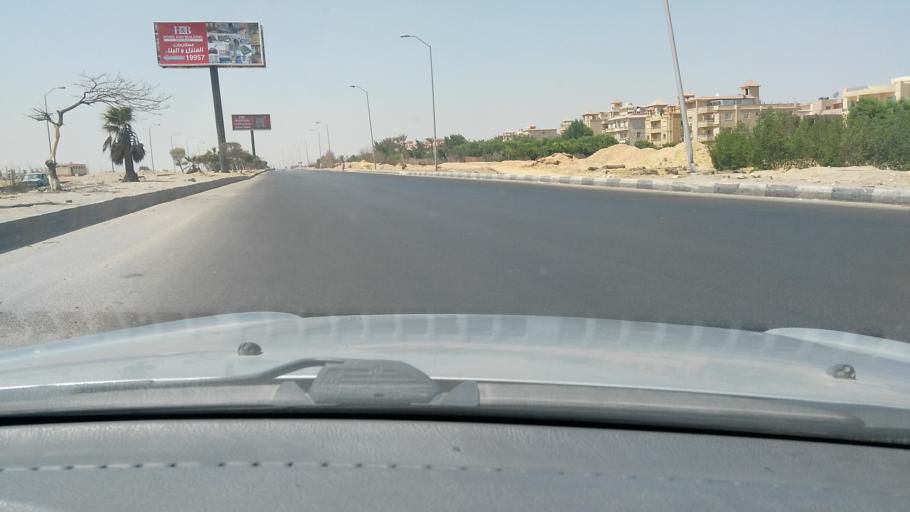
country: EG
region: Al Jizah
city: Madinat Sittah Uktubar
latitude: 29.9685
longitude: 30.9792
